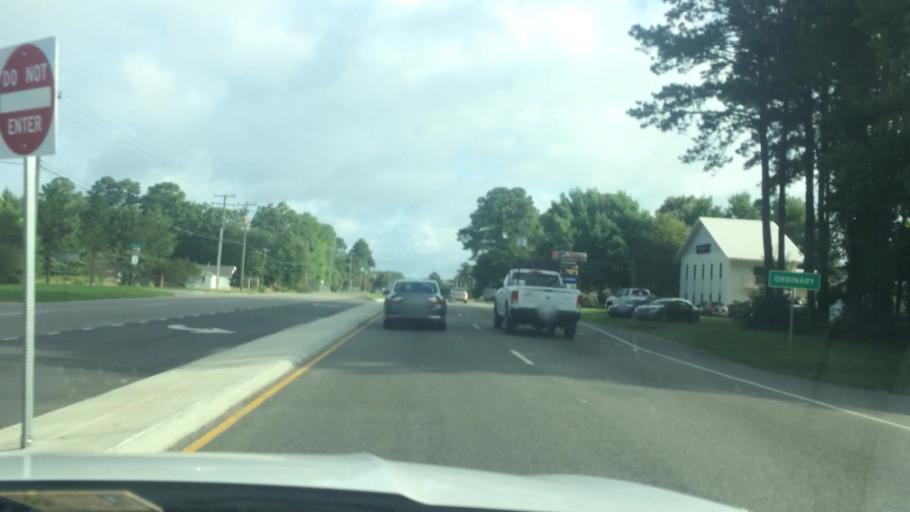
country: US
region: Virginia
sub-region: Gloucester County
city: Gloucester Point
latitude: 37.3168
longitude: -76.5135
